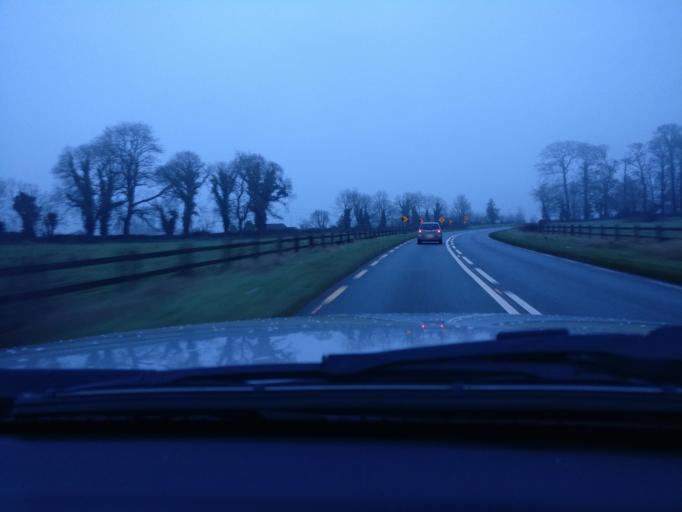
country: IE
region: Leinster
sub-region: An Mhi
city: Athboy
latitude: 53.6455
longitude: -6.8739
